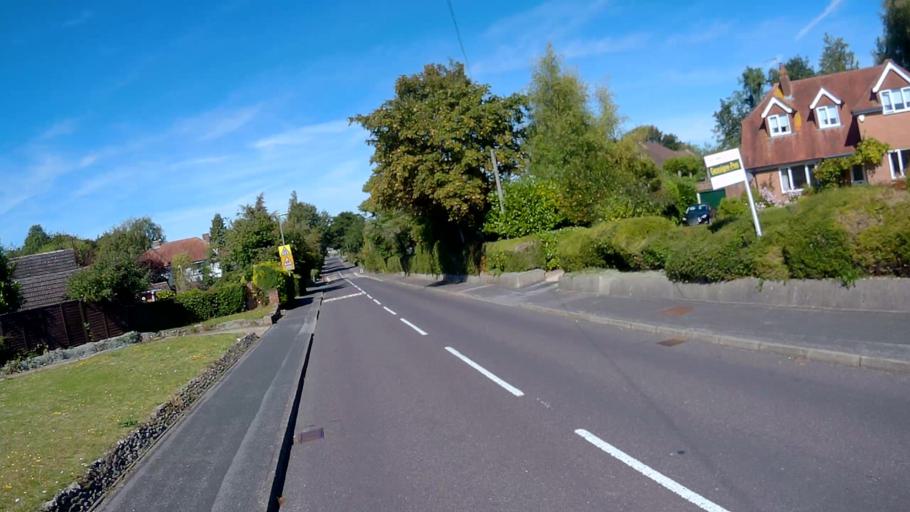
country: GB
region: England
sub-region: Hampshire
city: Basingstoke
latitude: 51.2451
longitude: -1.1352
